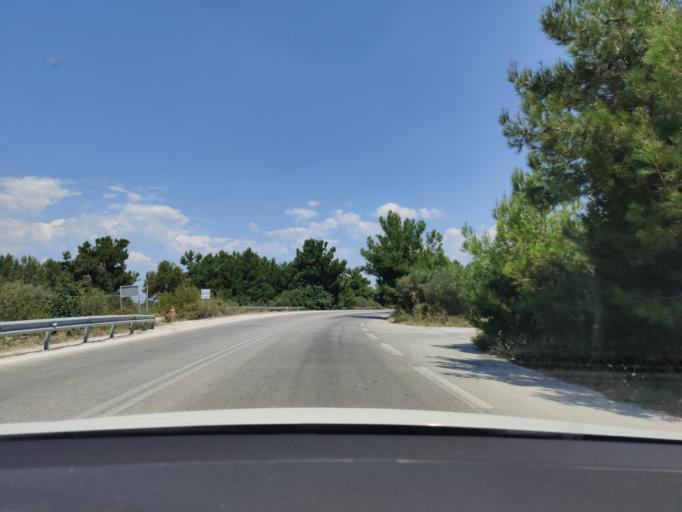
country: GR
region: East Macedonia and Thrace
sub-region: Nomos Kavalas
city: Prinos
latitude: 40.7602
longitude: 24.5911
